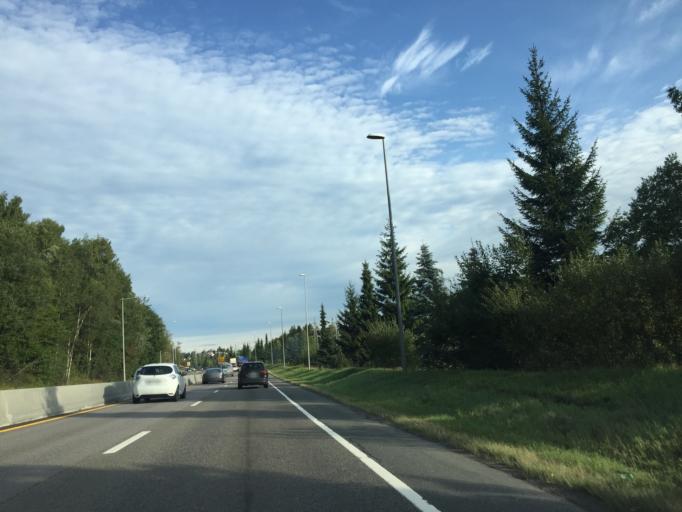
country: NO
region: Akershus
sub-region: Oppegard
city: Kolbotn
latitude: 59.8734
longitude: 10.8250
